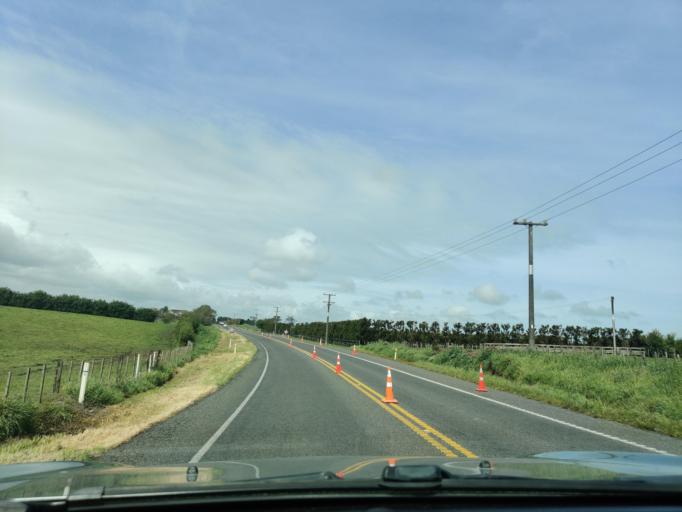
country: NZ
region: Taranaki
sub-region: South Taranaki District
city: Hawera
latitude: -39.6204
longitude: 174.3528
